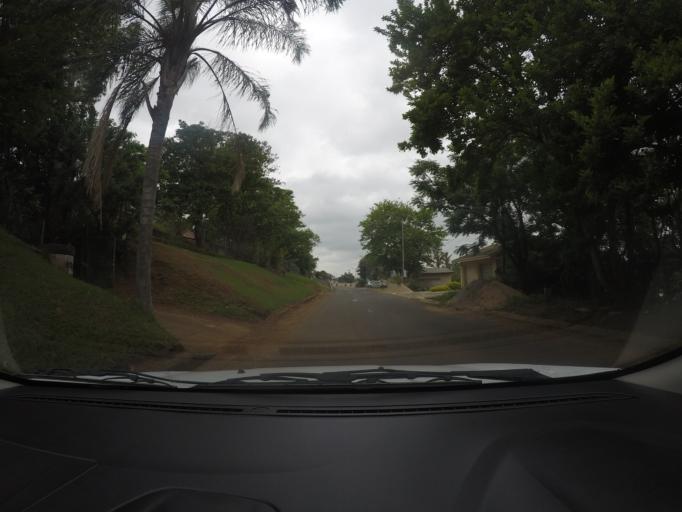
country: ZA
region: KwaZulu-Natal
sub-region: uThungulu District Municipality
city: Empangeni
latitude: -28.7468
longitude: 31.8940
